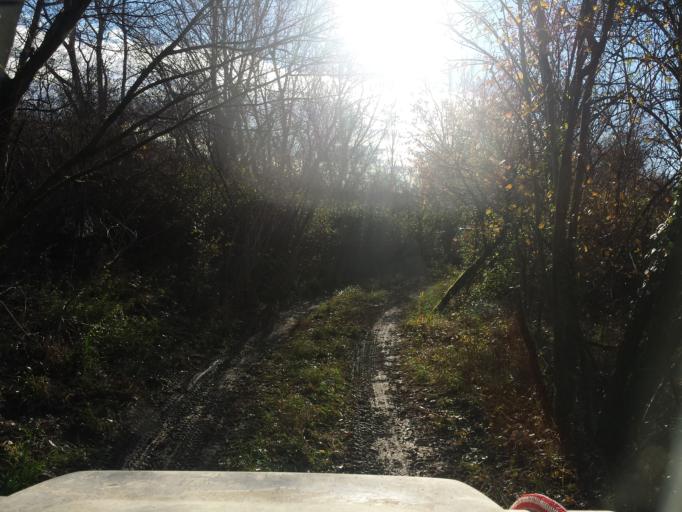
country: IT
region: Friuli Venezia Giulia
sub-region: Provincia di Gorizia
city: Villesse
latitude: 45.8704
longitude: 13.4230
